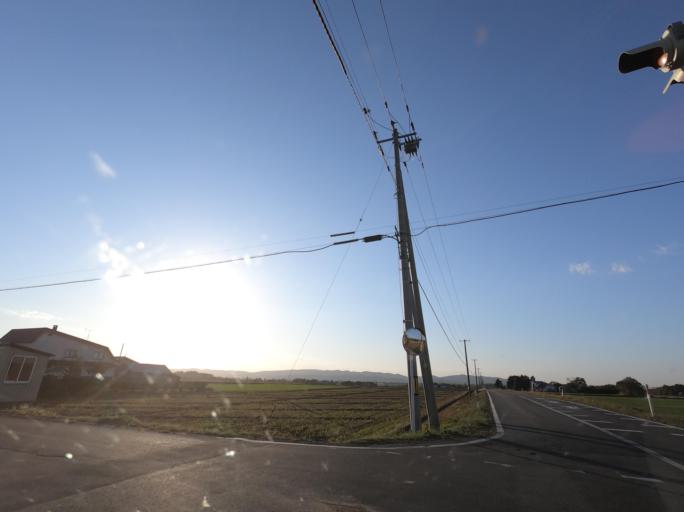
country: JP
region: Hokkaido
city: Iwamizawa
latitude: 42.9983
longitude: 141.8678
